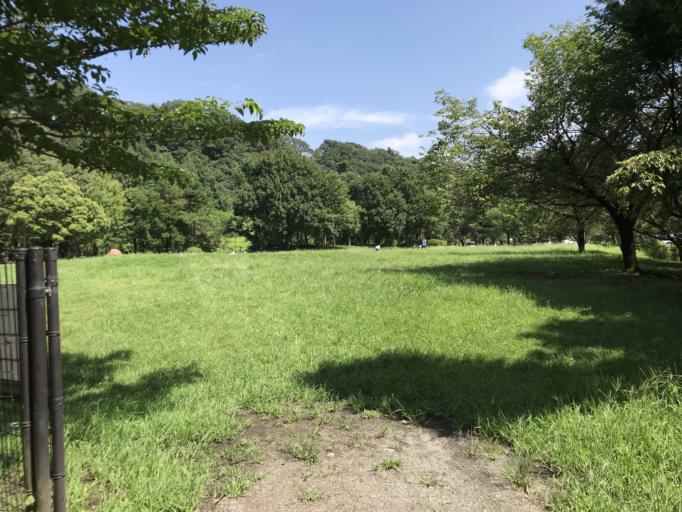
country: JP
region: Tokyo
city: Hachioji
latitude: 35.5750
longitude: 139.3104
